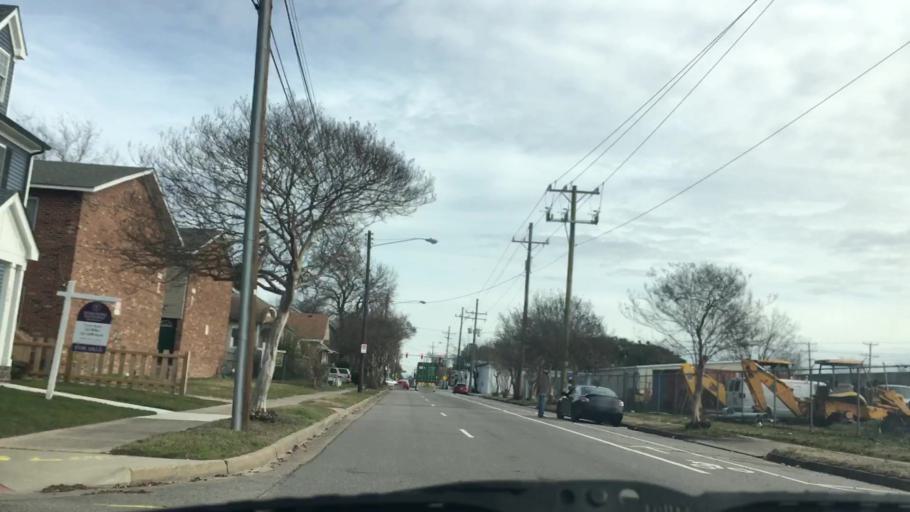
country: US
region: Virginia
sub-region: City of Norfolk
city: Norfolk
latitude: 36.8750
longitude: -76.2970
